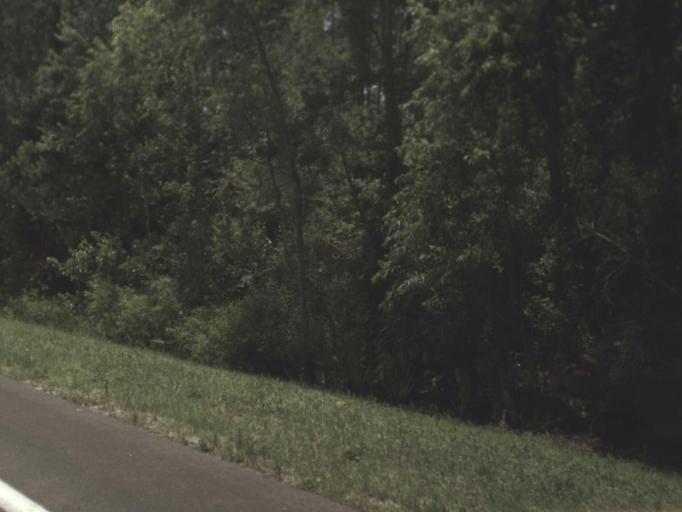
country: US
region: Florida
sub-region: Alachua County
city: Gainesville
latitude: 29.7223
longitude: -82.3541
